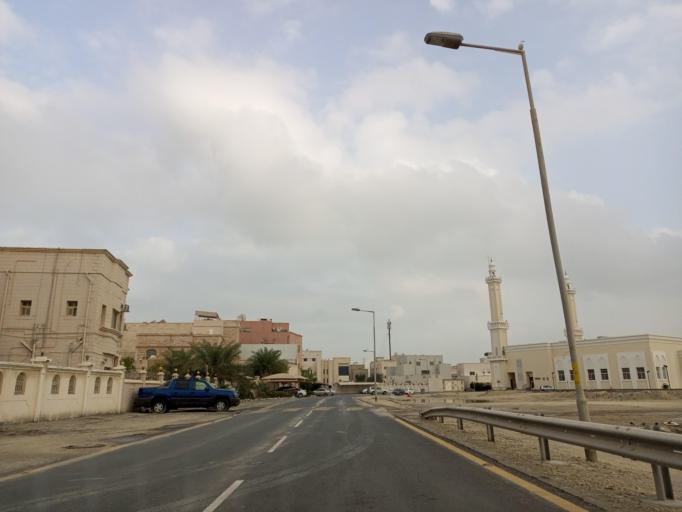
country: BH
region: Muharraq
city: Al Hadd
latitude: 26.2453
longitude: 50.6464
